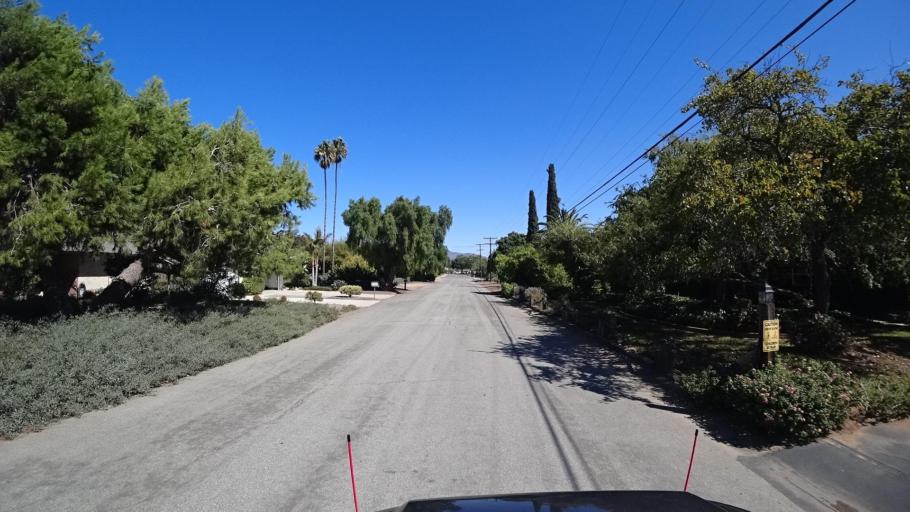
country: US
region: California
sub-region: San Diego County
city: Bonita
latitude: 32.6586
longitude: -117.0501
